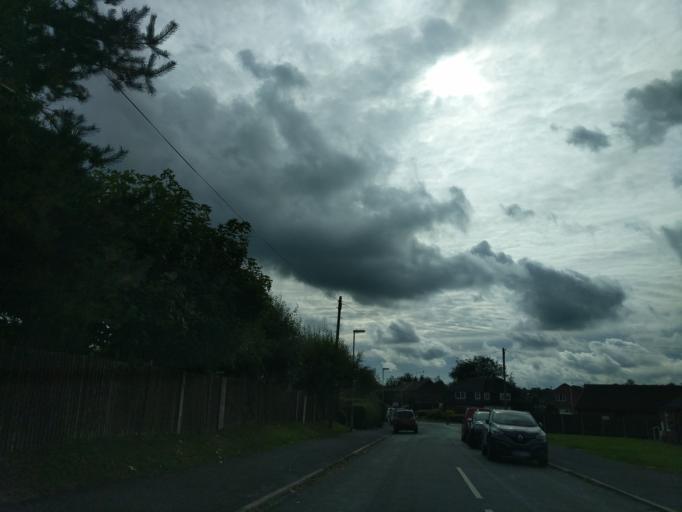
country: GB
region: England
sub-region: Staffordshire
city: Audley
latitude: 53.0003
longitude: -2.3444
